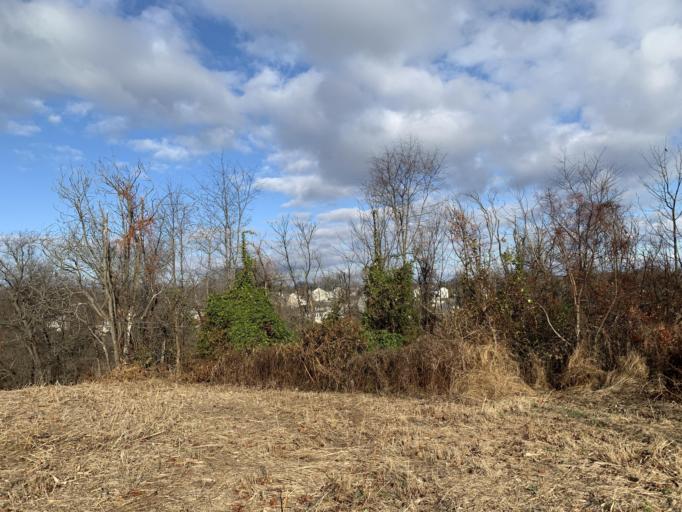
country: US
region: Pennsylvania
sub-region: Chester County
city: Kenilworth
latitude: 40.2014
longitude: -75.6062
